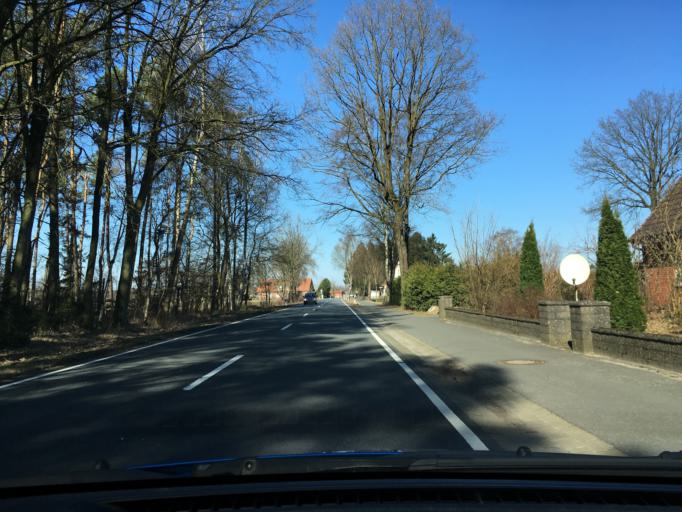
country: DE
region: Lower Saxony
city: Schneverdingen
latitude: 53.0818
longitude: 9.8072
